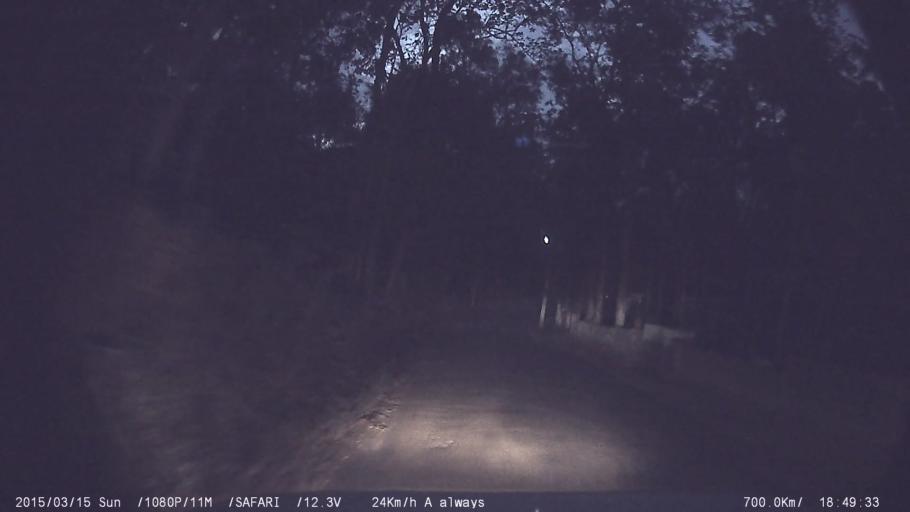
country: IN
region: Kerala
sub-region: Kottayam
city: Palackattumala
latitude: 9.8554
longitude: 76.6970
